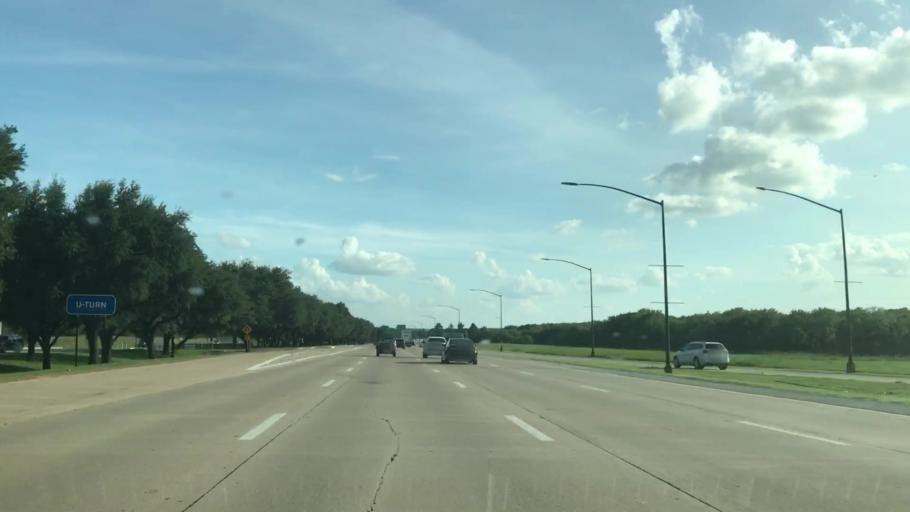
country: US
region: Texas
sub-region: Tarrant County
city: Euless
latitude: 32.8502
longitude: -97.0410
